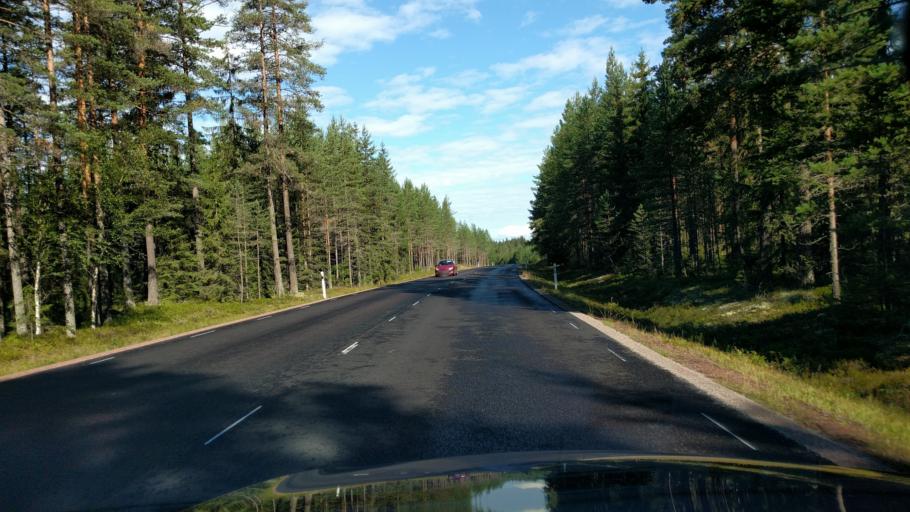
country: SE
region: Dalarna
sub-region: Alvdalens Kommun
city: AElvdalen
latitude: 61.1631
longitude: 14.1160
